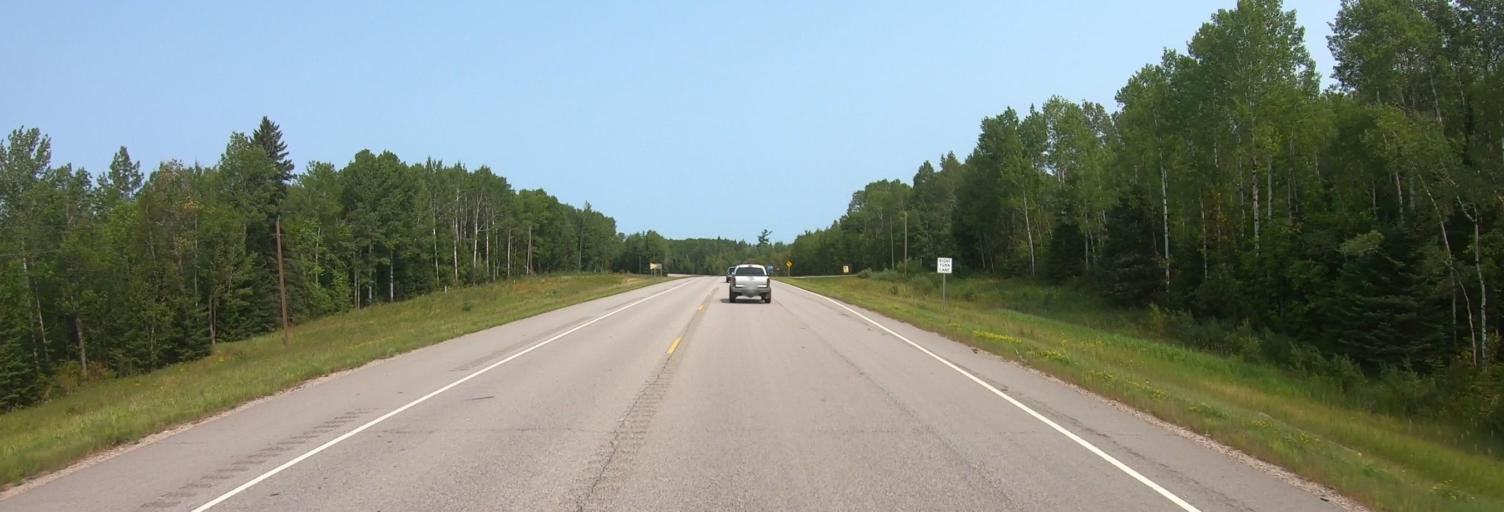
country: CA
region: Ontario
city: Fort Frances
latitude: 48.3604
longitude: -92.9632
